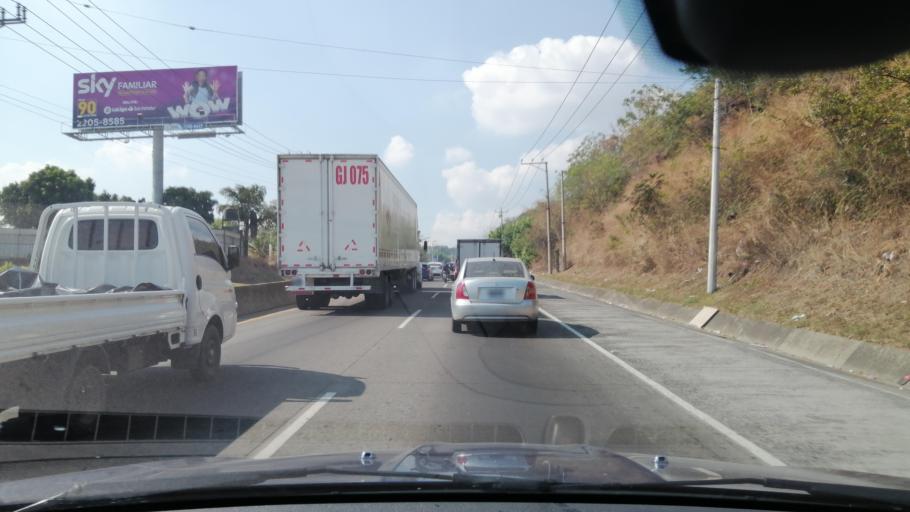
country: SV
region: San Salvador
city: Ayutuxtepeque
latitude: 13.7554
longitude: -89.2166
